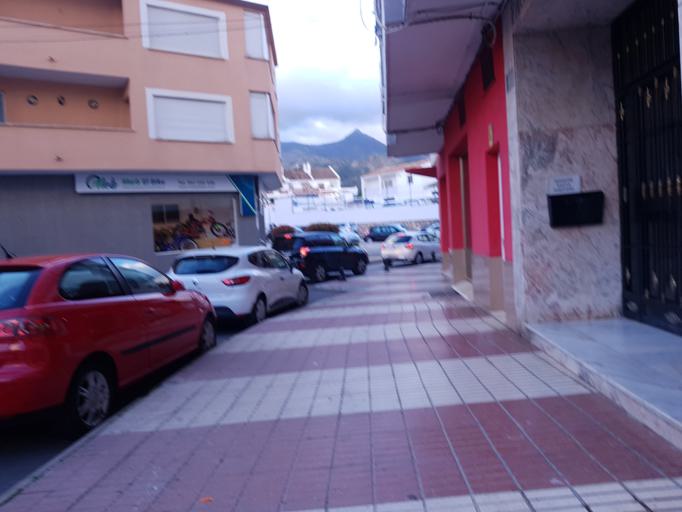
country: ES
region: Andalusia
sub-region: Provincia de Malaga
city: Marbella
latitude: 36.5170
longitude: -4.8875
